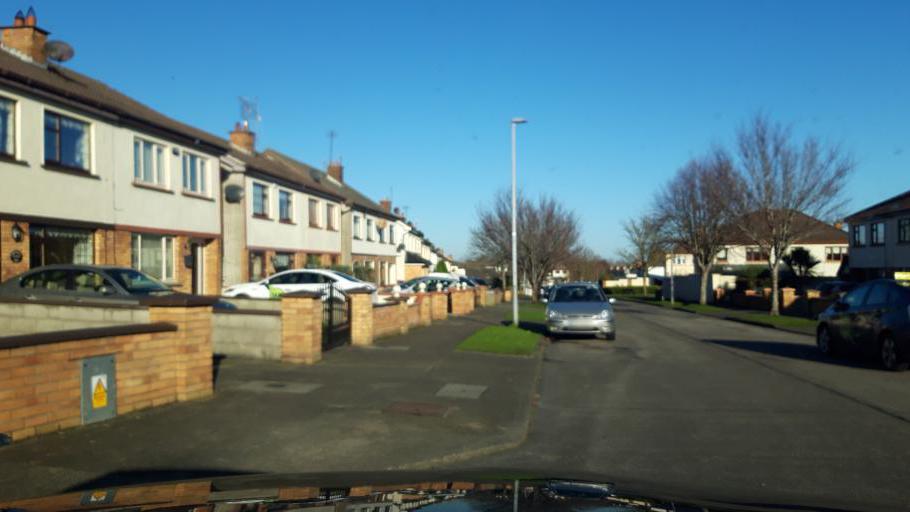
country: IE
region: Leinster
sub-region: Fingal County
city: Swords
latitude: 53.4519
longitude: -6.2492
